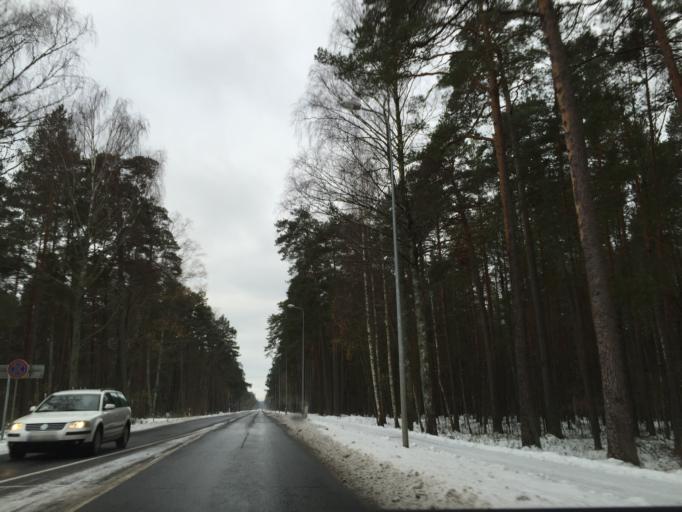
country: LV
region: Saulkrastu
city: Saulkrasti
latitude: 57.2508
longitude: 24.4095
